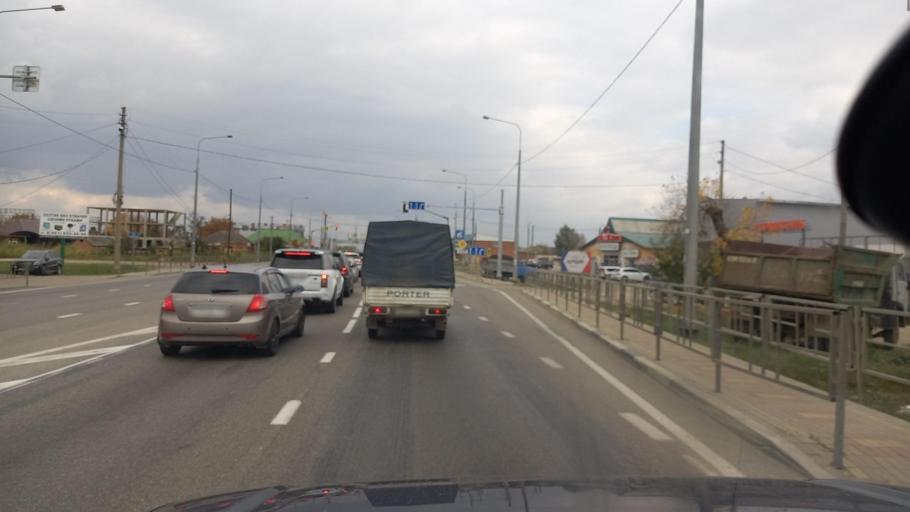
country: RU
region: Adygeya
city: Enem
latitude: 44.9296
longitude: 38.9097
